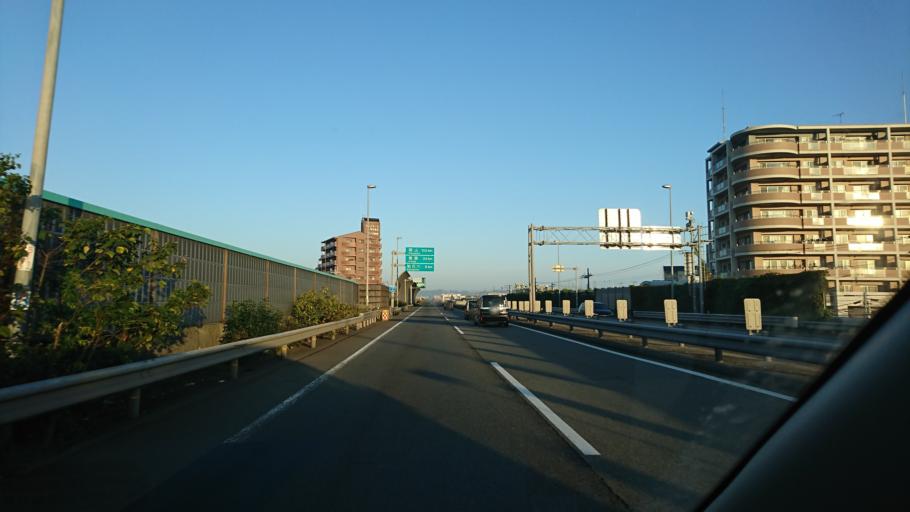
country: JP
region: Hyogo
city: Kakogawacho-honmachi
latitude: 34.7239
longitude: 134.8947
